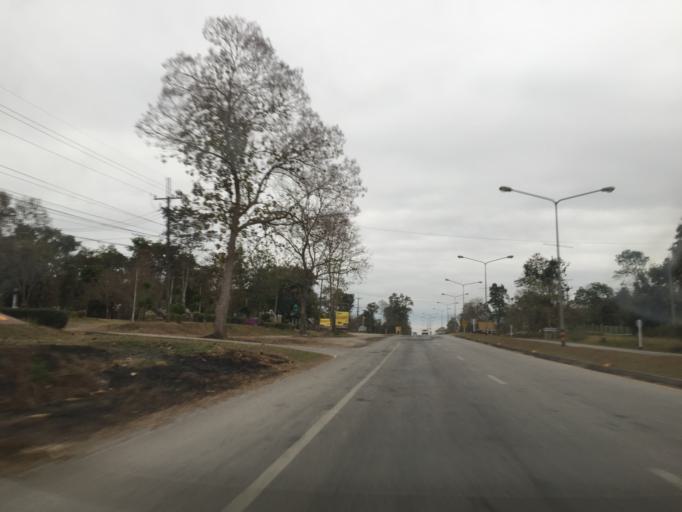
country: TH
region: Loei
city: Erawan
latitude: 17.3075
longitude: 101.9392
